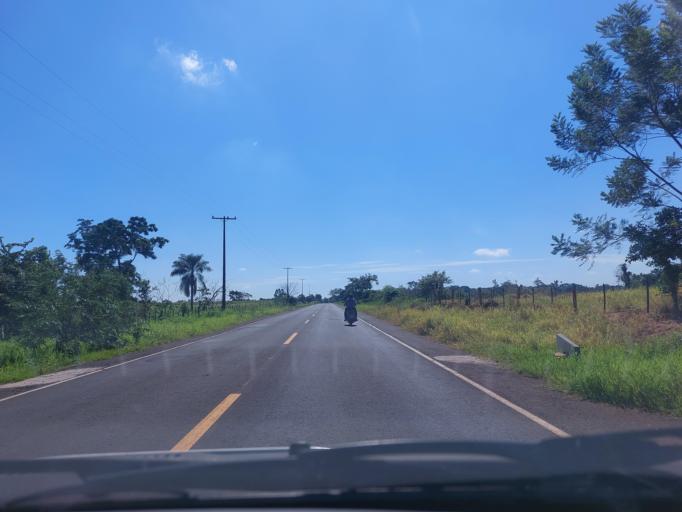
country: PY
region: San Pedro
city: Guayaybi
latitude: -24.5762
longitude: -56.5196
